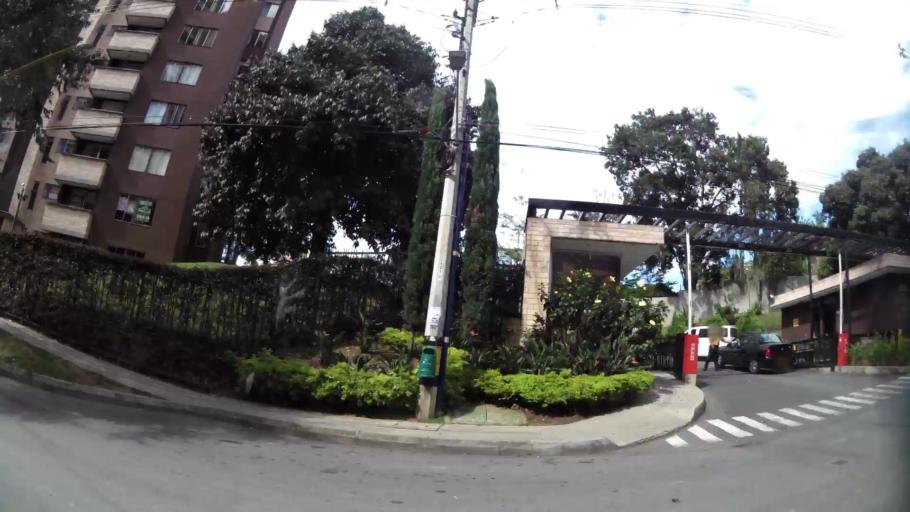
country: CO
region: Antioquia
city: Sabaneta
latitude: 6.1513
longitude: -75.6102
